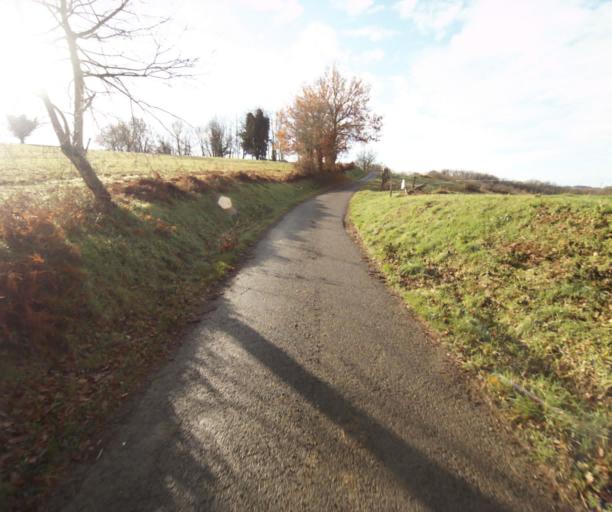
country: FR
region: Limousin
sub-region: Departement de la Correze
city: Sainte-Fereole
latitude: 45.2511
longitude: 1.6056
